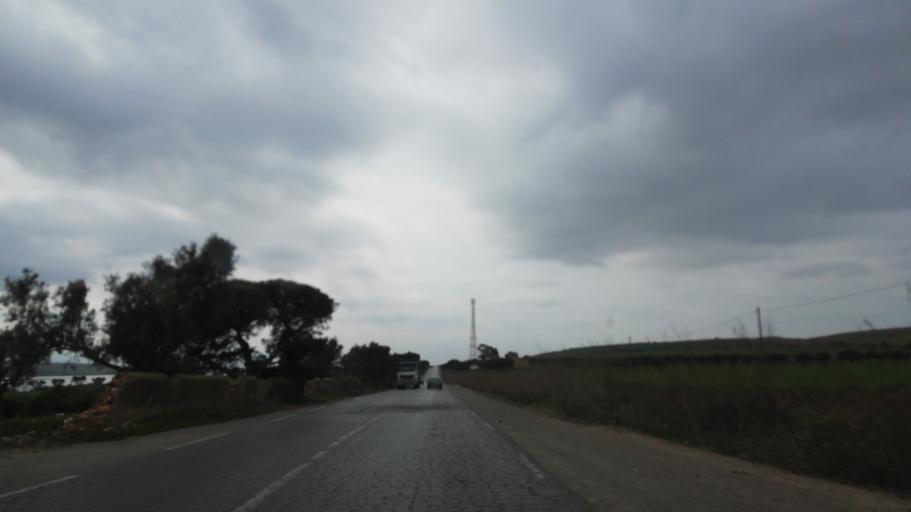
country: DZ
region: Oran
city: Sidi ech Chahmi
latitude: 35.6136
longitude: -0.4223
